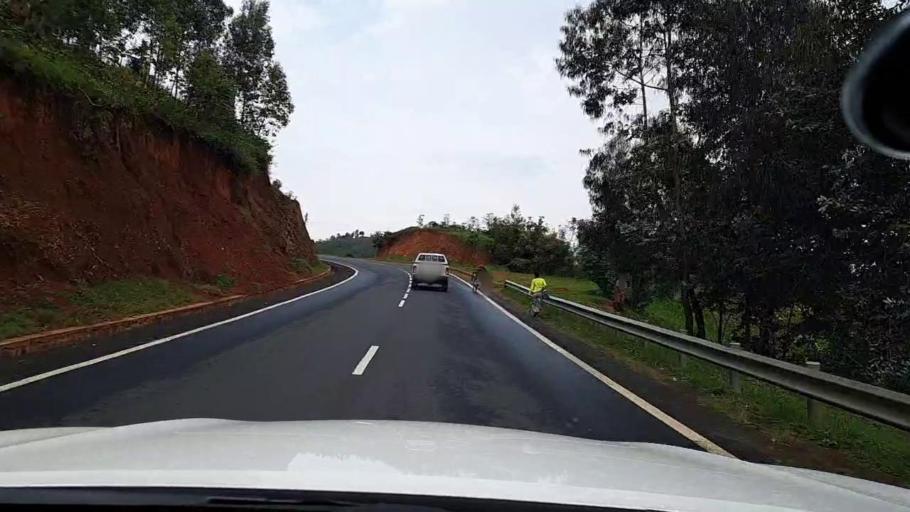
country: RW
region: Western Province
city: Kibuye
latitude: -2.1653
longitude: 29.2933
